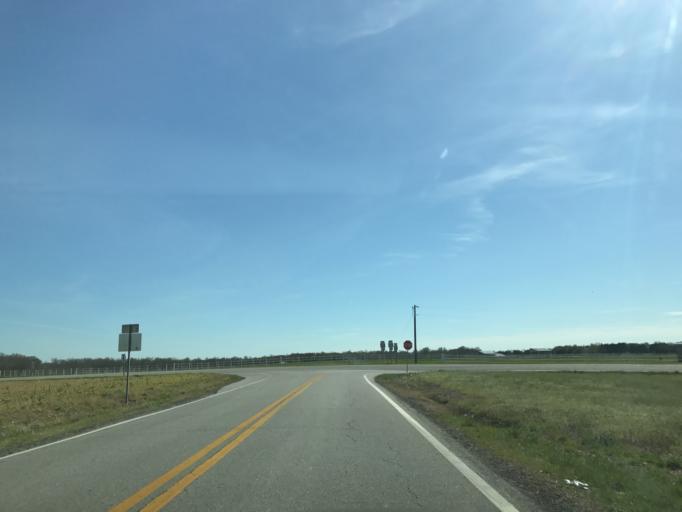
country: US
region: Maryland
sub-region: Caroline County
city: Ridgely
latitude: 38.9466
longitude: -75.9806
